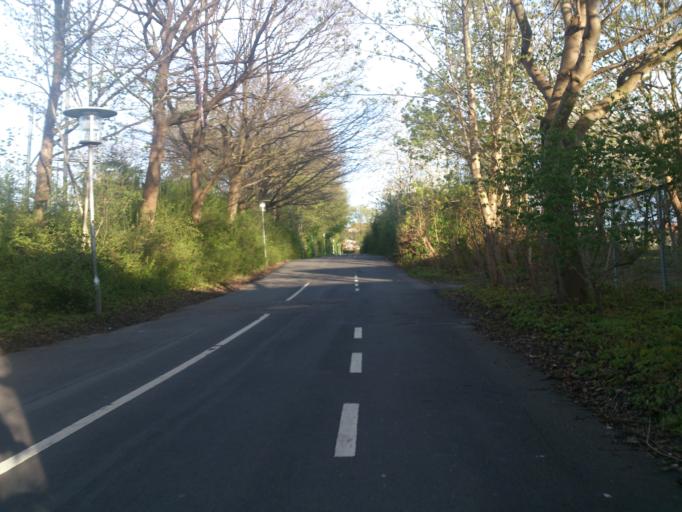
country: DK
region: Capital Region
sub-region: Ballerup Kommune
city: Ballerup
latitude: 55.7316
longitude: 12.3526
